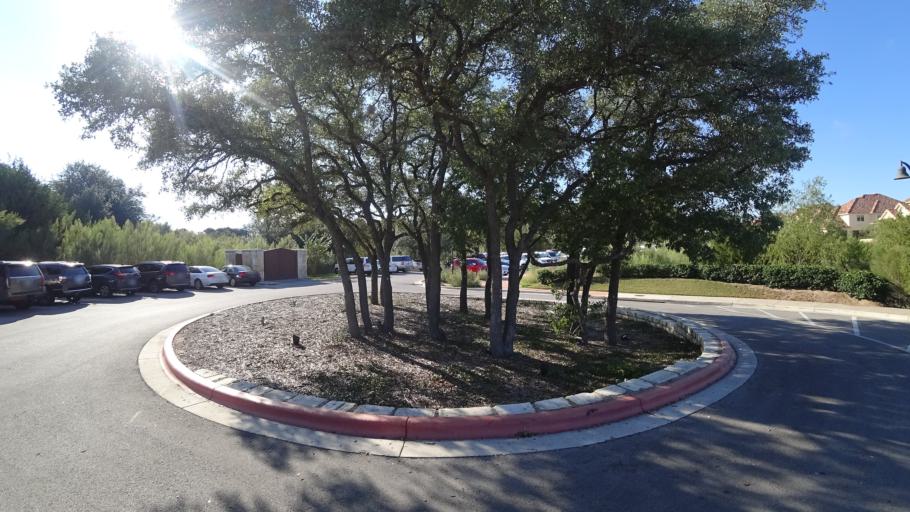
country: US
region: Texas
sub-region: Travis County
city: Hudson Bend
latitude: 30.3595
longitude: -97.8906
